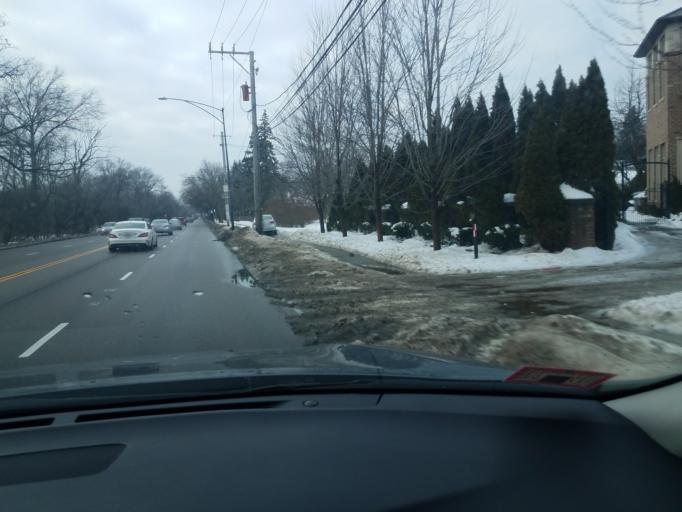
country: US
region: Illinois
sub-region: Cook County
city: Niles
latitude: 42.0028
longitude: -87.7783
